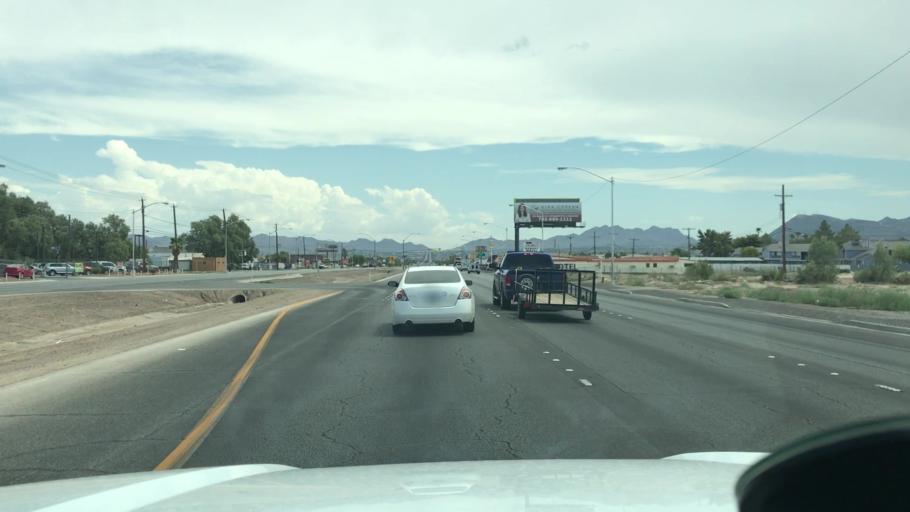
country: US
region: Nevada
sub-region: Clark County
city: Whitney
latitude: 36.0941
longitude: -115.0436
